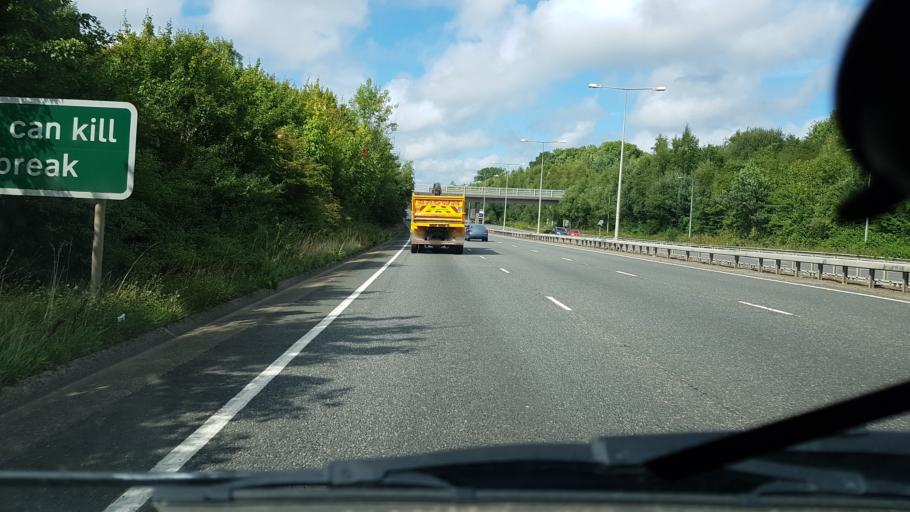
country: GB
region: England
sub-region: West Sussex
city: Broadfield
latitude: 51.0587
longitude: -0.2027
